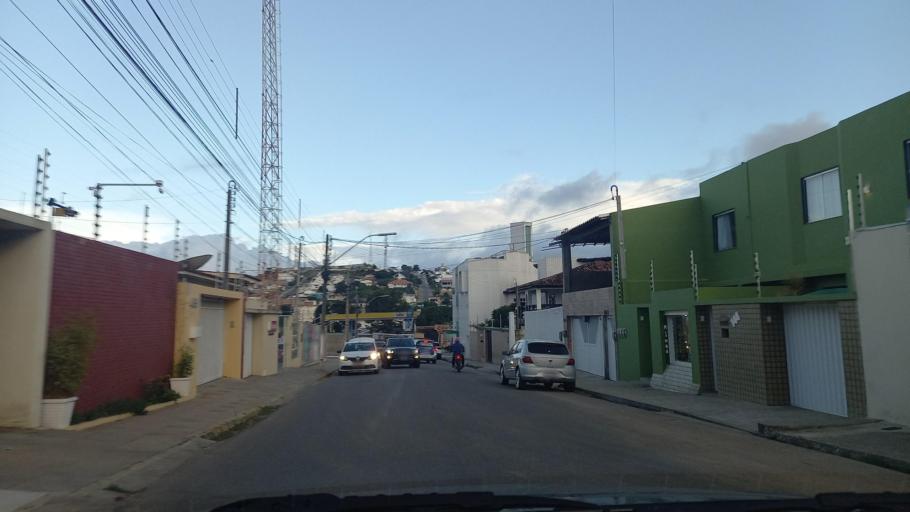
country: BR
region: Pernambuco
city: Garanhuns
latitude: -8.8822
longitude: -36.4749
